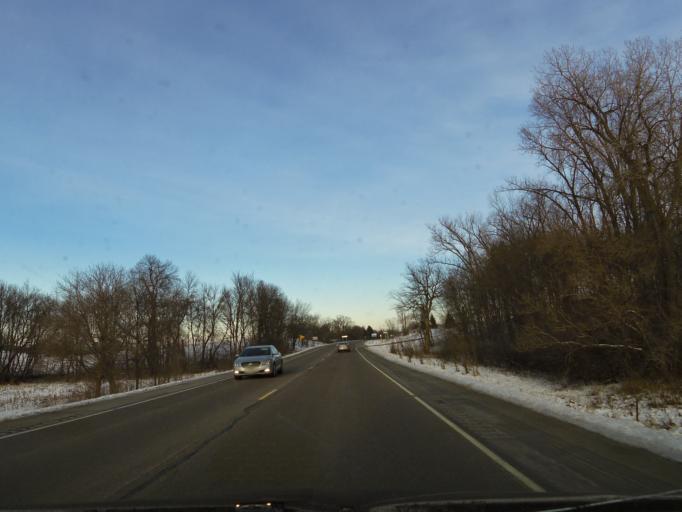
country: US
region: Wisconsin
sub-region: Polk County
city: Osceola
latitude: 45.3172
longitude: -92.7401
